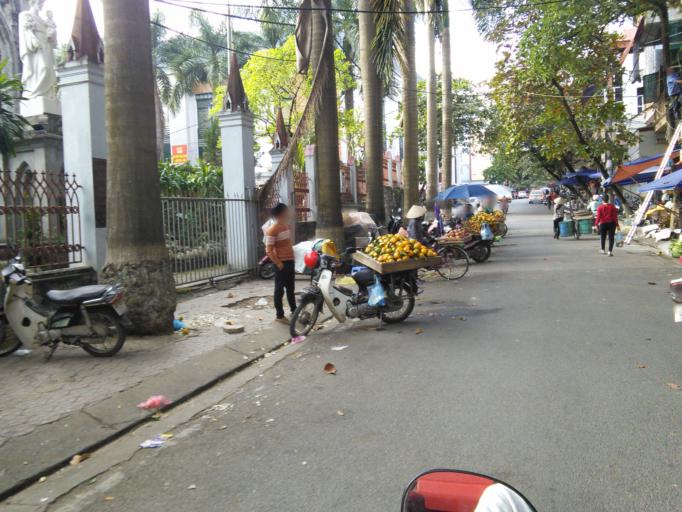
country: VN
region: Lao Cai
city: Lao Cai
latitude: 22.5004
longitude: 103.9685
